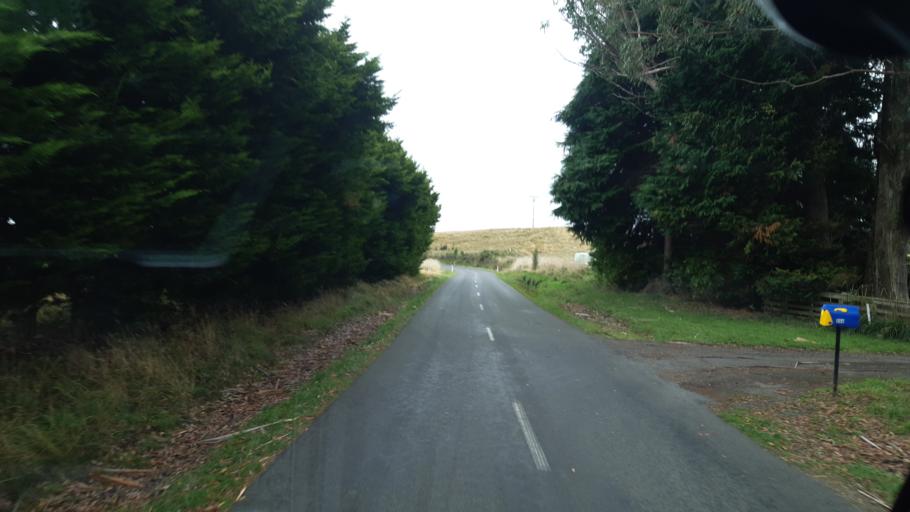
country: NZ
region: Manawatu-Wanganui
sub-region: Ruapehu District
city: Waiouru
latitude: -39.5485
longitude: 175.6587
